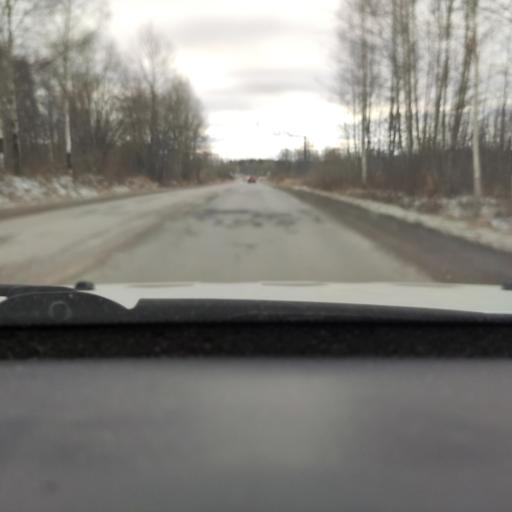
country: RU
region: Perm
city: Perm
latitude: 58.0972
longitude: 56.4060
